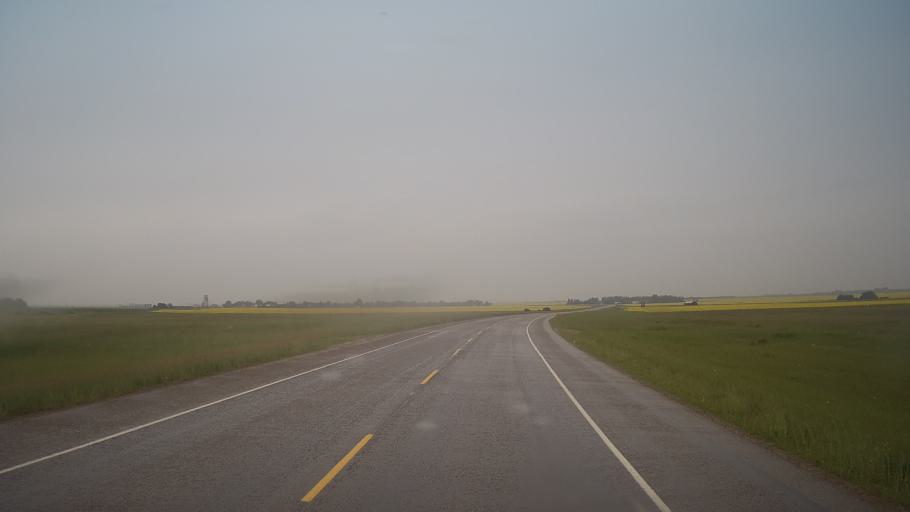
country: CA
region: Saskatchewan
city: Wilkie
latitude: 52.1921
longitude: -108.4238
